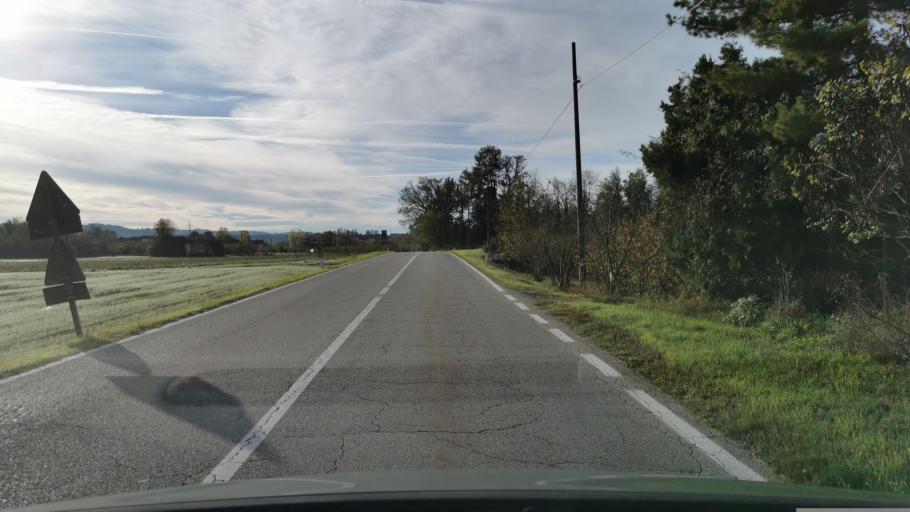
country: IT
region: Piedmont
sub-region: Provincia di Cuneo
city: Narzole
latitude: 44.5915
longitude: 7.8941
